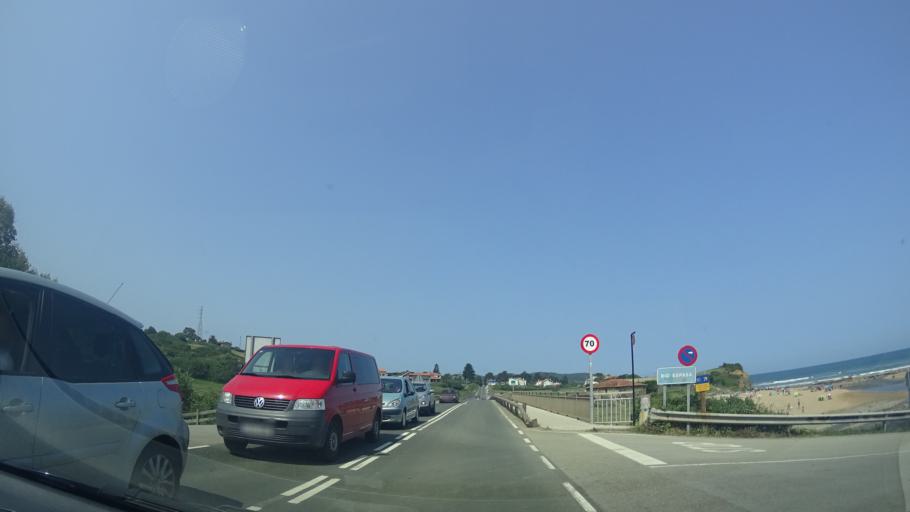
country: ES
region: Asturias
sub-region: Province of Asturias
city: Colunga
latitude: 43.4729
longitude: -5.2156
